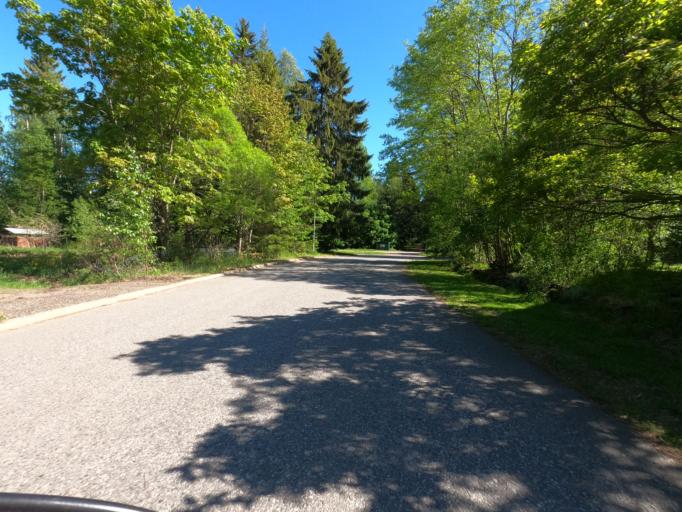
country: FI
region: North Karelia
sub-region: Joensuu
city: Joensuu
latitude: 62.5914
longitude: 29.7983
